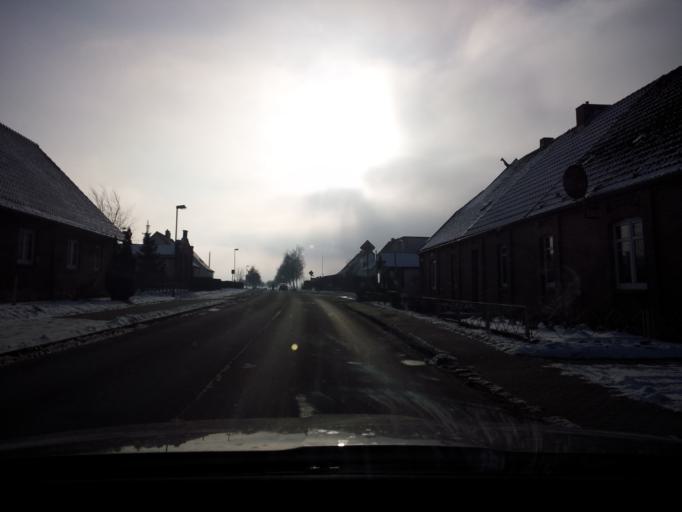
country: DE
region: Mecklenburg-Vorpommern
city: Blowatz
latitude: 53.9608
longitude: 11.4894
